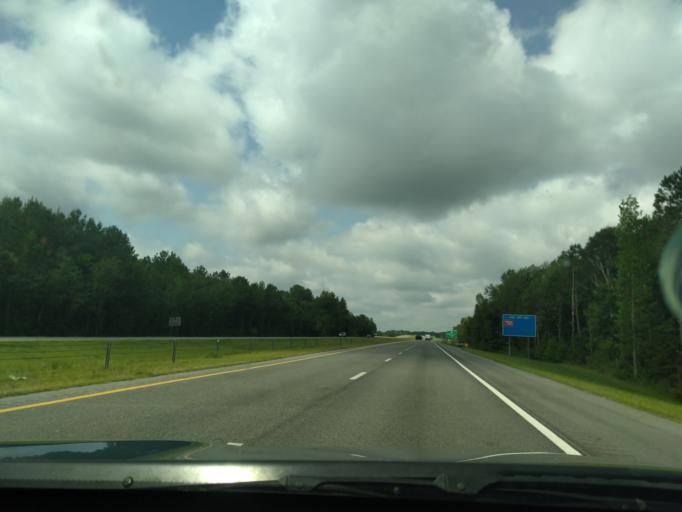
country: US
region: North Carolina
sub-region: Martin County
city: Robersonville
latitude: 35.8400
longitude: -77.2415
